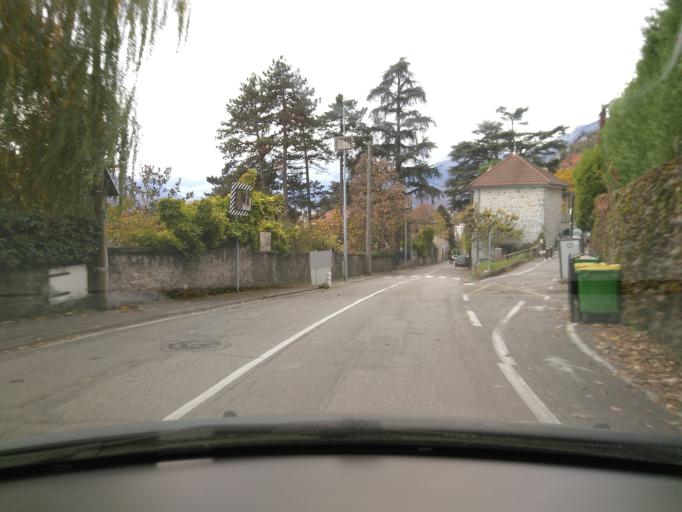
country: FR
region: Rhone-Alpes
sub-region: Departement de l'Isere
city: La Tronche
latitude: 45.2079
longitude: 5.7416
